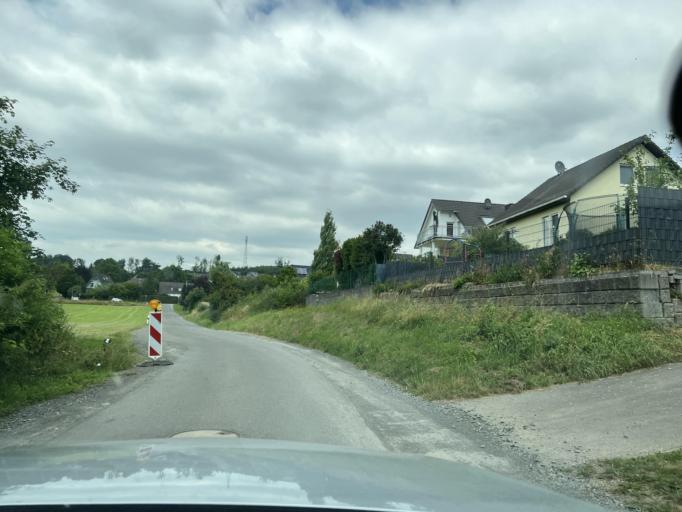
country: DE
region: North Rhine-Westphalia
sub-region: Regierungsbezirk Koln
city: Lindlar
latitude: 51.0153
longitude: 7.3586
